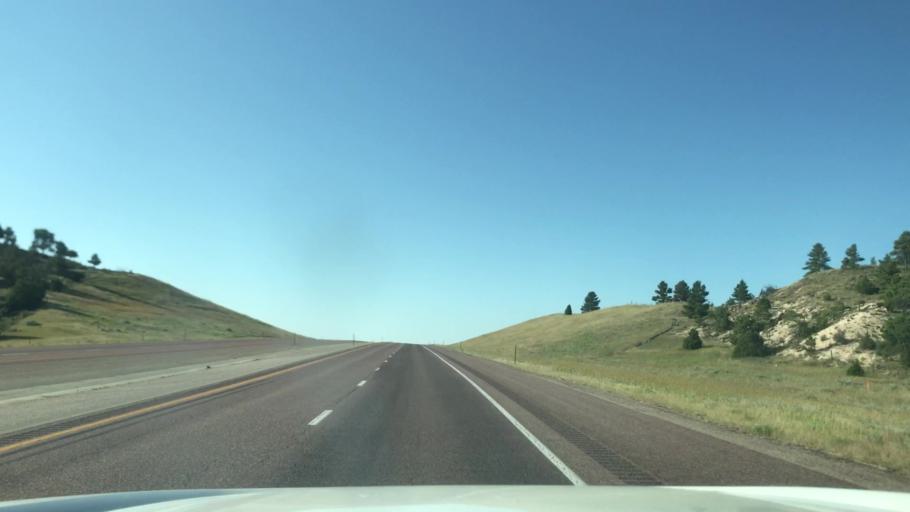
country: US
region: Wyoming
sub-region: Platte County
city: Guernsey
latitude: 42.4501
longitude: -105.0351
